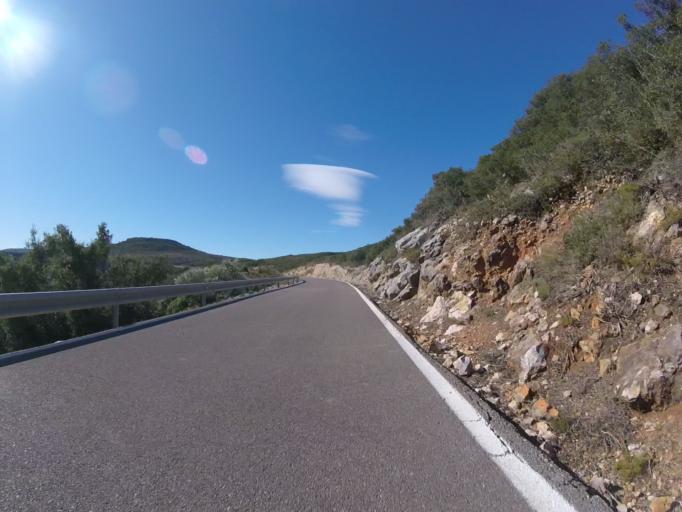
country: ES
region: Valencia
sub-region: Provincia de Castello
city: Albocasser
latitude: 40.3954
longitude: 0.0412
